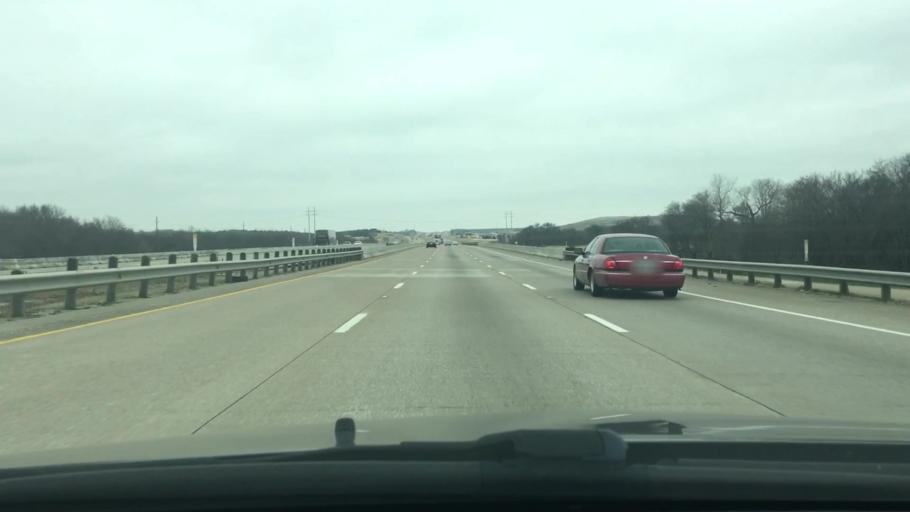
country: US
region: Texas
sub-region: Ellis County
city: Palmer
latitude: 32.4100
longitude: -96.6590
